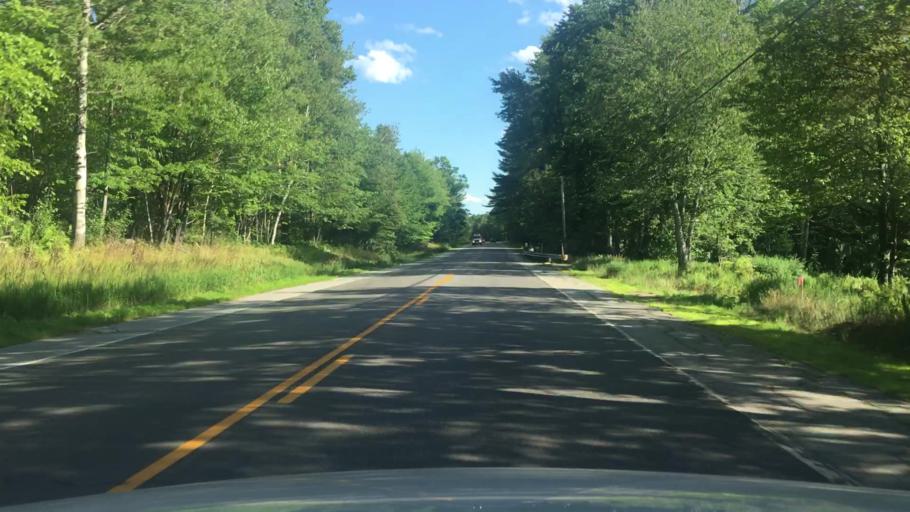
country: US
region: Maine
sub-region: Franklin County
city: Jay
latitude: 44.5373
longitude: -70.2341
